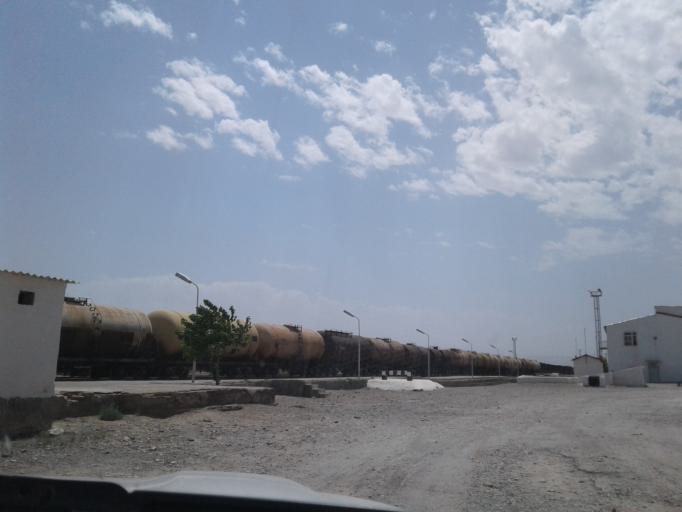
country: IR
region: Razavi Khorasan
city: Kalat-e Naderi
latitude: 37.2005
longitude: 60.0312
